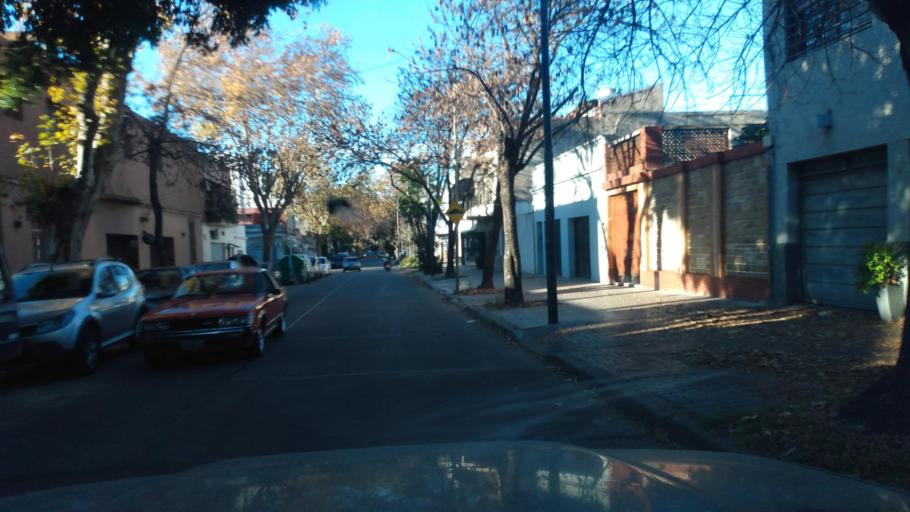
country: AR
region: Buenos Aires F.D.
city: Villa Santa Rita
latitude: -34.5847
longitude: -58.4832
